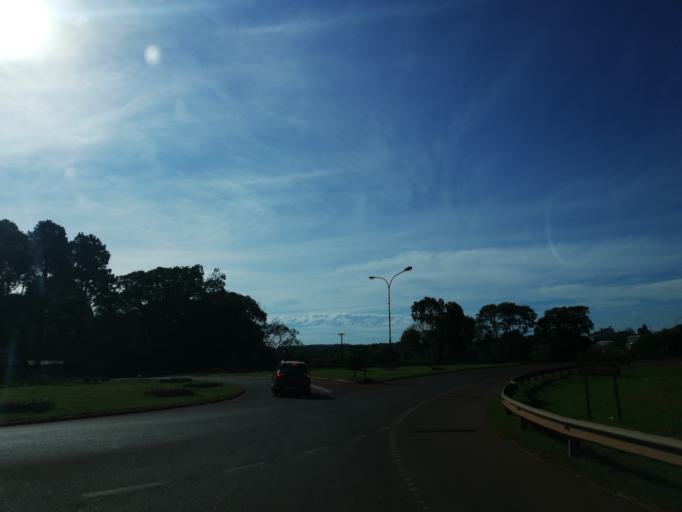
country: AR
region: Misiones
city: Dos de Mayo
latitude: -26.9992
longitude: -54.4944
